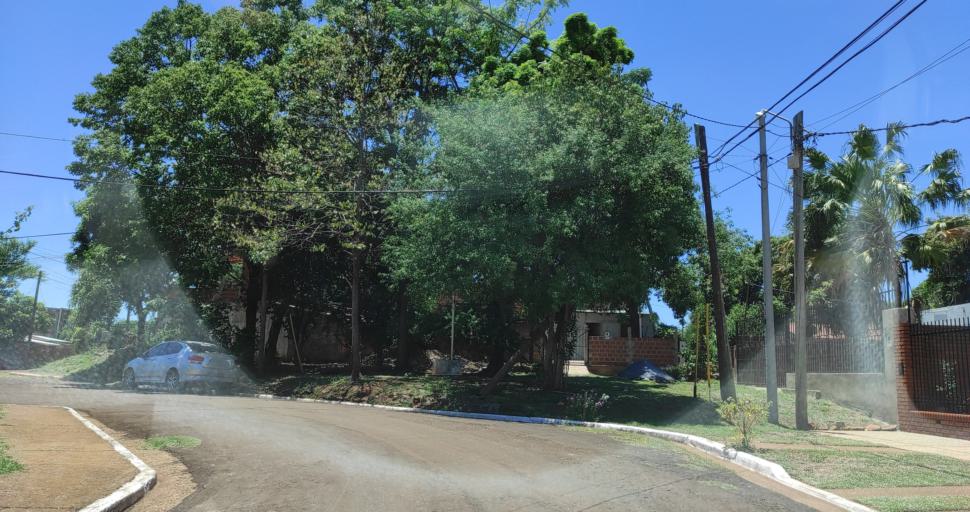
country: AR
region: Misiones
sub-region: Departamento de Capital
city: Posadas
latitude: -27.4068
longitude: -55.9075
